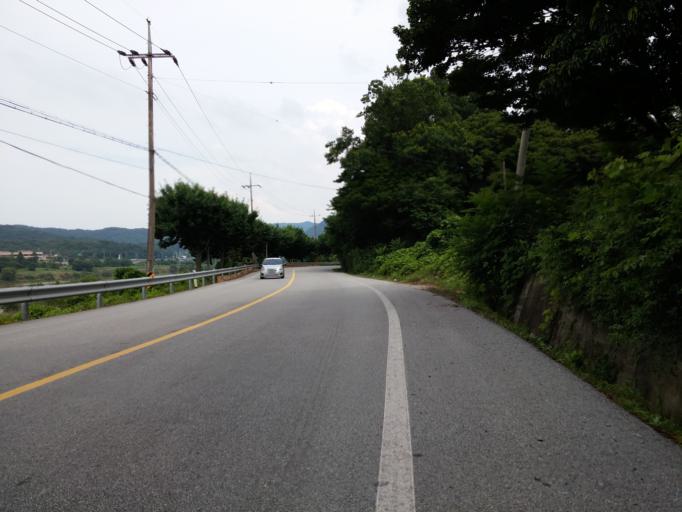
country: KR
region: Chungcheongnam-do
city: Gongju
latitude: 36.4433
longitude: 127.1888
